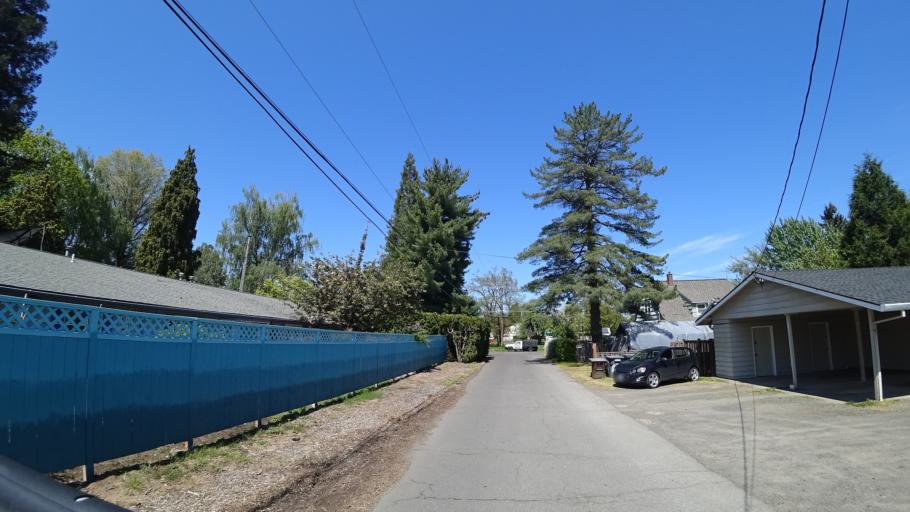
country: US
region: Oregon
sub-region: Washington County
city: Hillsboro
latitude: 45.5182
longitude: -122.9720
